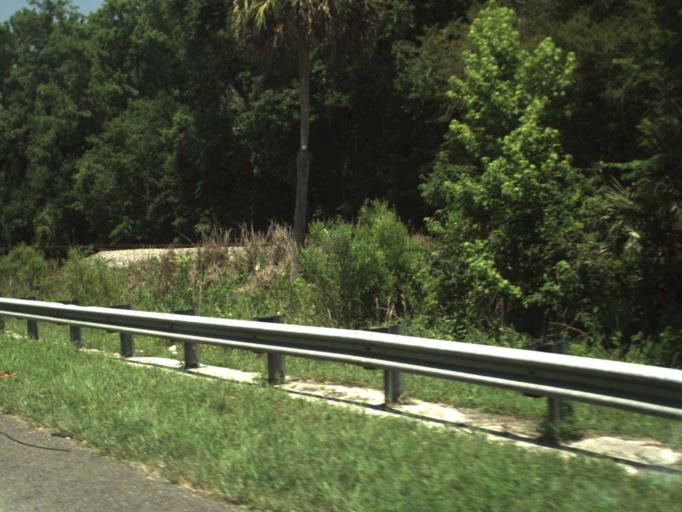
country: US
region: Florida
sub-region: Seminole County
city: Winter Springs
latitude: 28.7185
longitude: -81.3086
